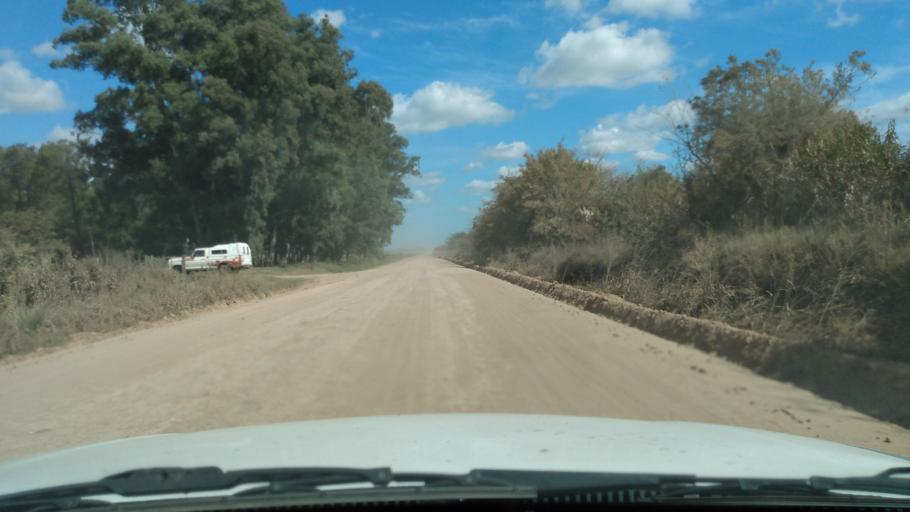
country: AR
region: Buenos Aires
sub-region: Partido de Navarro
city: Navarro
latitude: -35.0242
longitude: -59.4375
